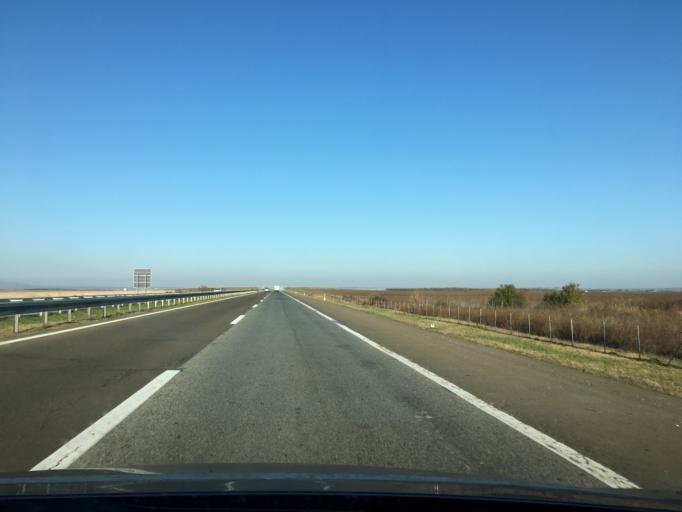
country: RS
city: Novi Karlovci
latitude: 45.0813
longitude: 20.1372
